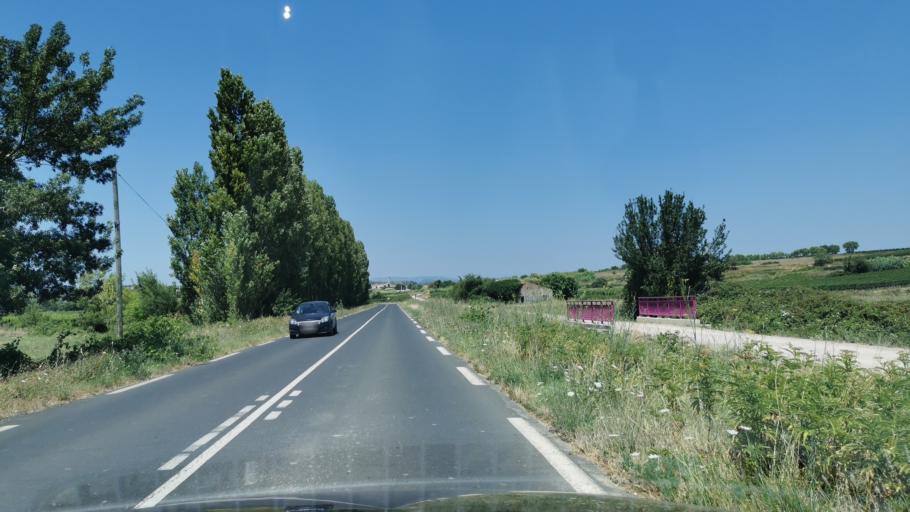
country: FR
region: Languedoc-Roussillon
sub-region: Departement de l'Herault
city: Cazouls-les-Beziers
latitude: 43.3780
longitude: 3.1103
